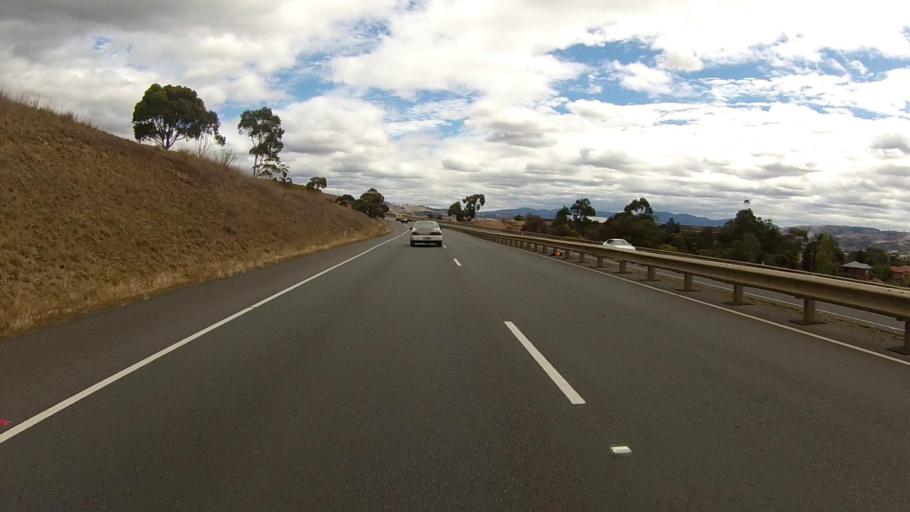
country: AU
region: Tasmania
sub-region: Glenorchy
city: Austins Ferry
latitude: -42.7661
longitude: 147.2350
